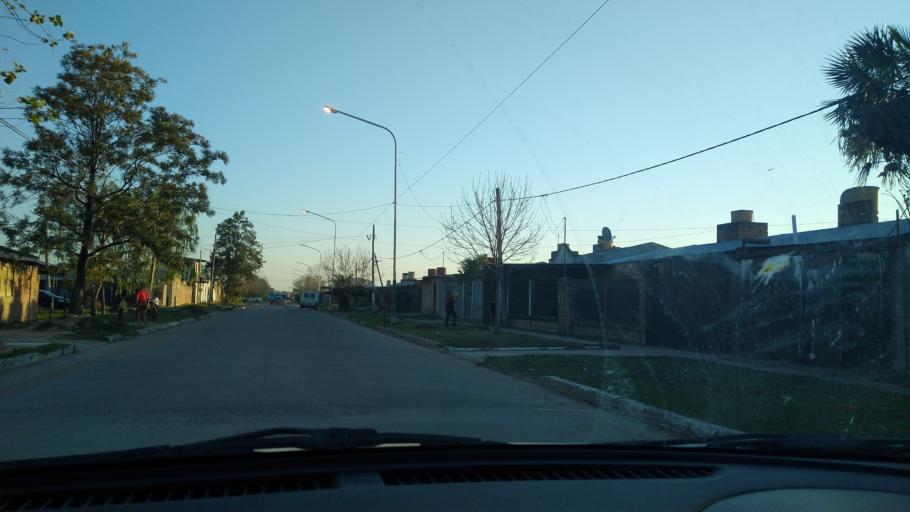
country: AR
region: Chaco
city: Puerto Vilelas
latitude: -27.5106
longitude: -58.9444
